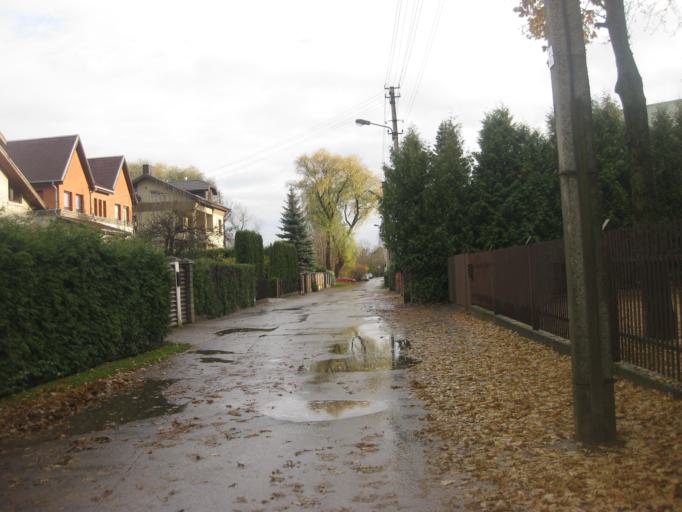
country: LT
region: Kauno apskritis
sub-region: Kaunas
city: Aleksotas
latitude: 54.8592
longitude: 23.8863
